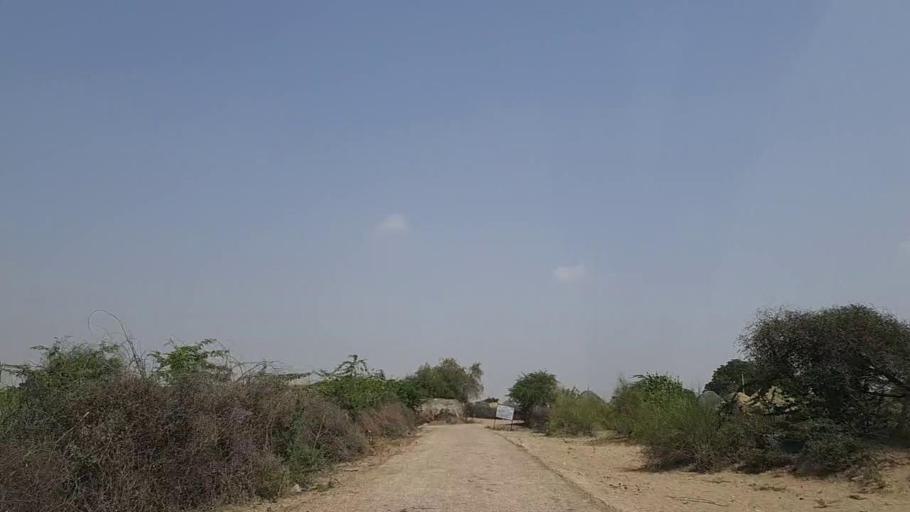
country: PK
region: Sindh
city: Mithi
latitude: 24.7604
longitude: 69.9299
